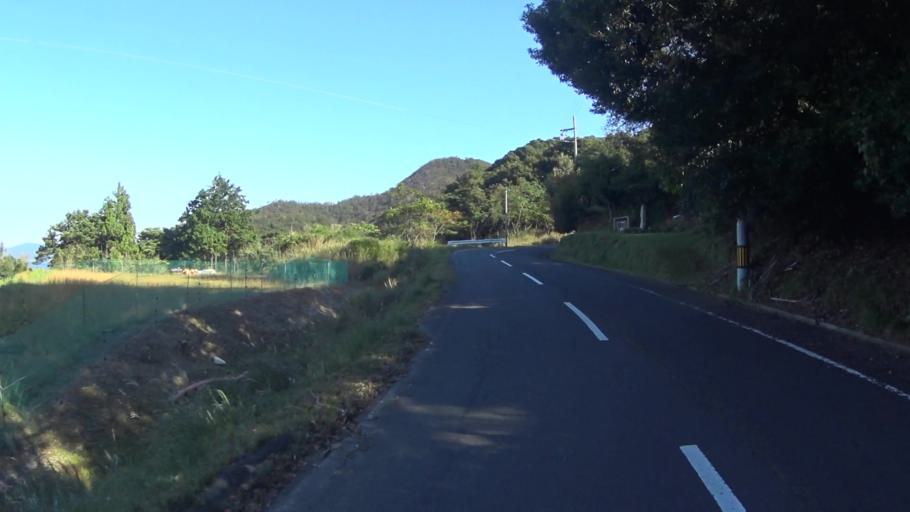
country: JP
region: Hyogo
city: Toyooka
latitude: 35.6474
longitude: 134.8820
